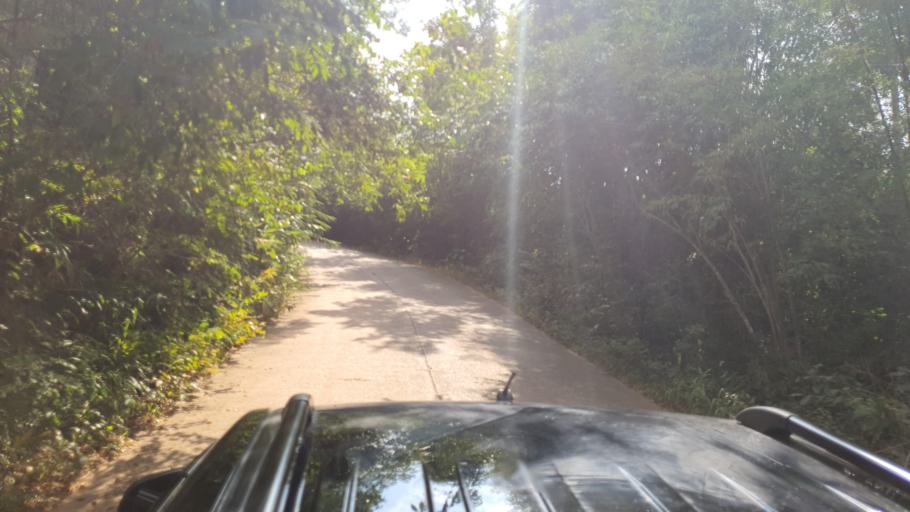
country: TH
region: Changwat Bueng Kan
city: Si Wilai
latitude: 18.2740
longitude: 103.7962
